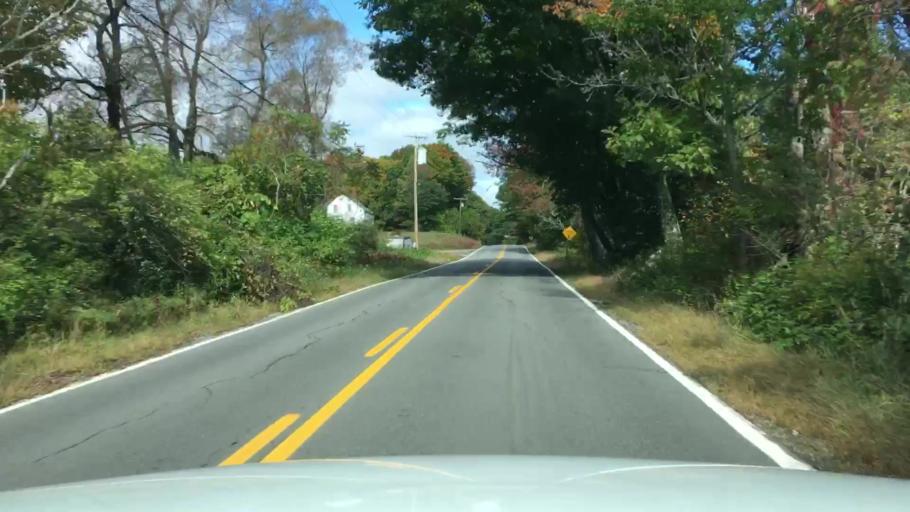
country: US
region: Maine
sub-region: Sagadahoc County
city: North Bath
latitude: 43.9776
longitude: -69.8899
